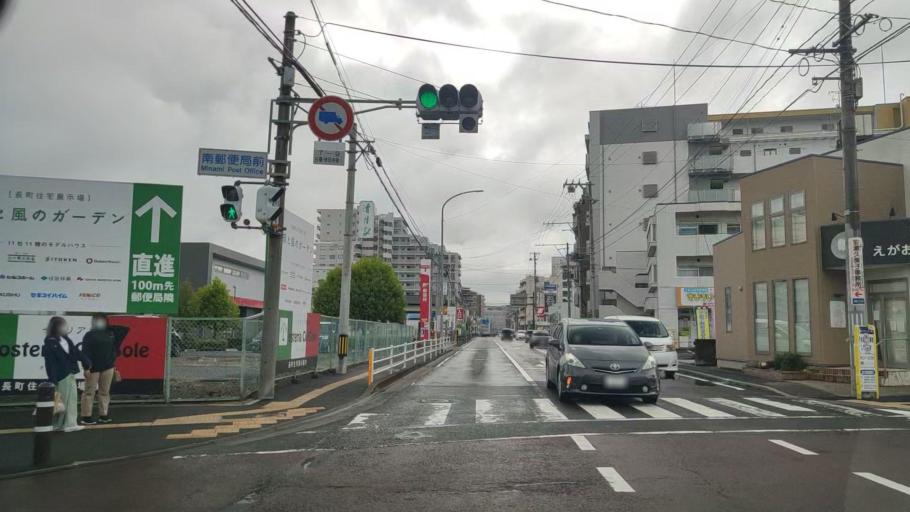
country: JP
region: Miyagi
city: Sendai
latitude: 38.2282
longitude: 140.8774
